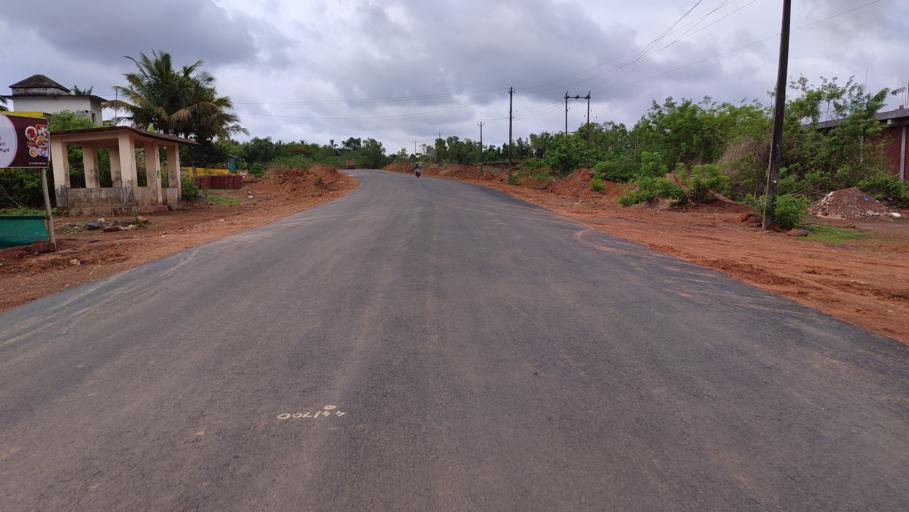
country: IN
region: Kerala
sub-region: Kasaragod District
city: Kasaragod
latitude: 12.5557
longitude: 75.0701
